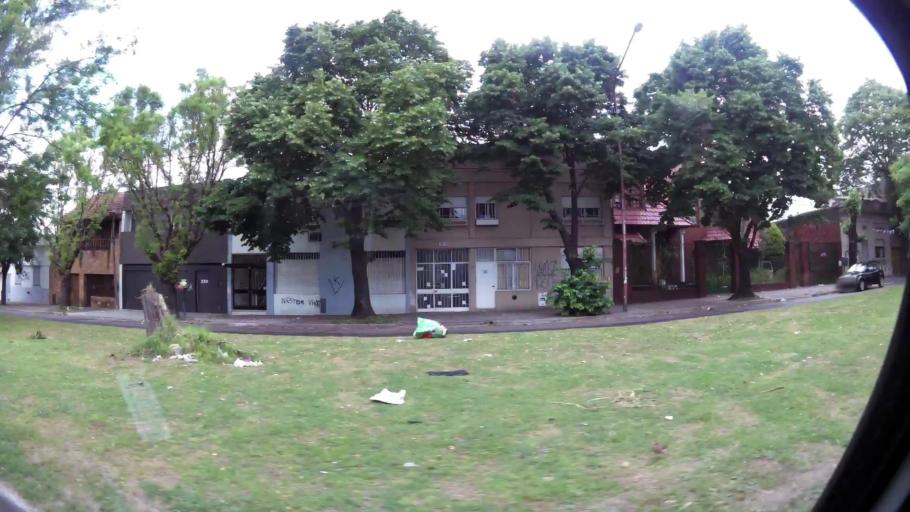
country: AR
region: Buenos Aires
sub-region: Partido de La Plata
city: La Plata
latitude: -34.9149
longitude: -57.9280
